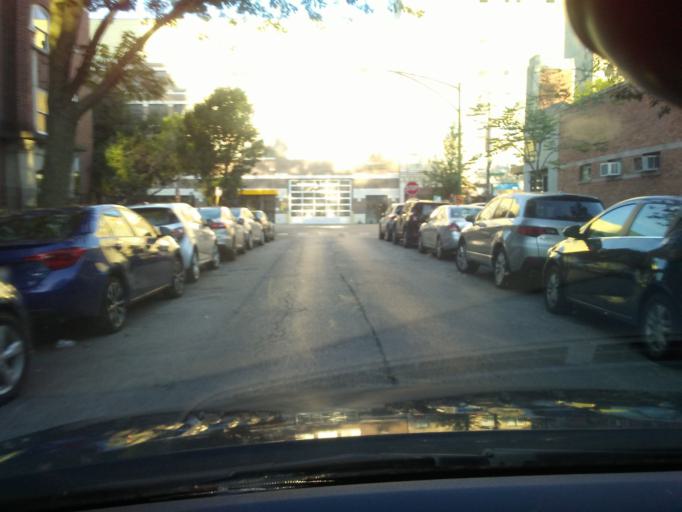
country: US
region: Illinois
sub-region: Cook County
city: Evanston
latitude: 41.9743
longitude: -87.6544
